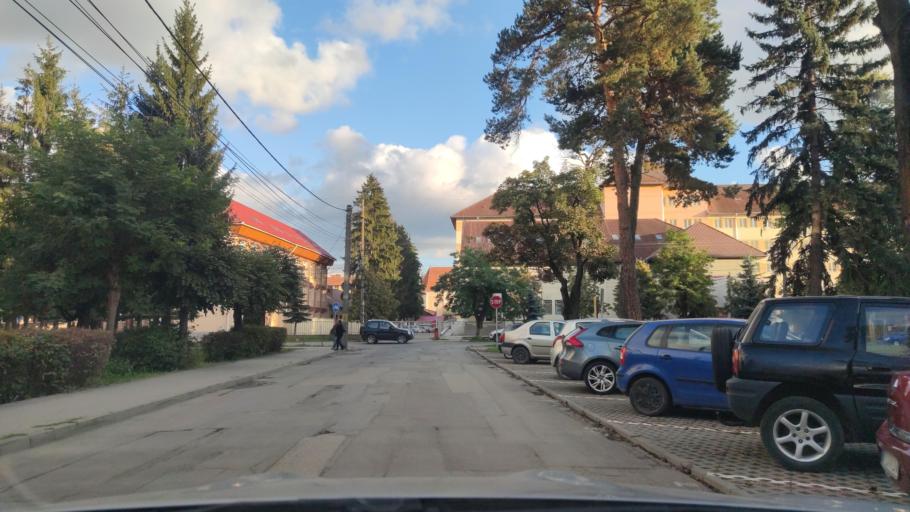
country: RO
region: Harghita
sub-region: Municipiul Gheorgheni
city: Gheorgheni
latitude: 46.7242
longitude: 25.6021
